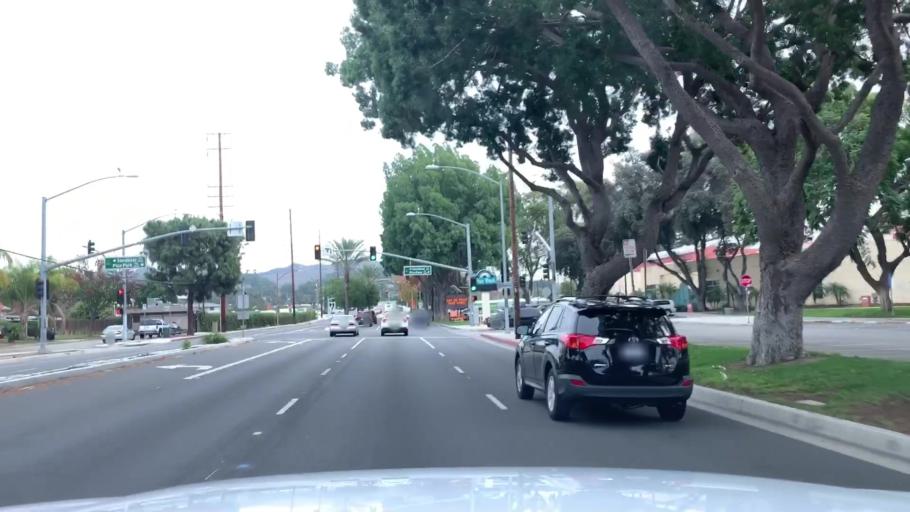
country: US
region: California
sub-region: Los Angeles County
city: Montebello
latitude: 34.0083
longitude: -118.0738
